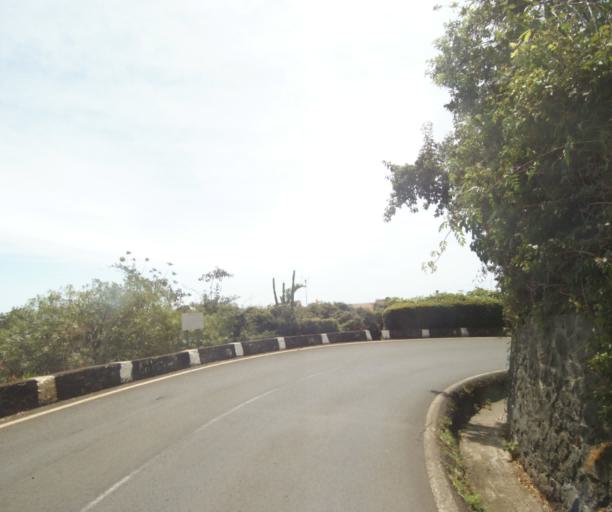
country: RE
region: Reunion
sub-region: Reunion
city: Saint-Paul
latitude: -21.0456
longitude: 55.2877
